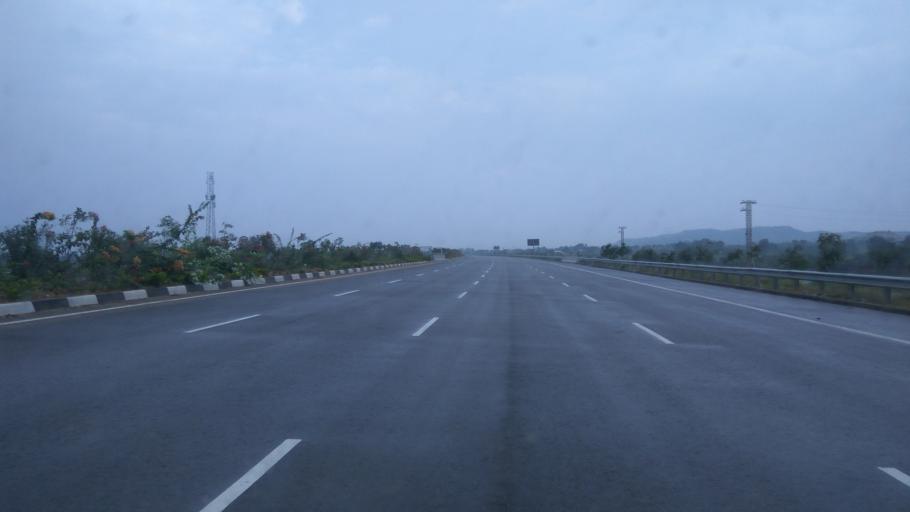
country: IN
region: Telangana
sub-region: Rangareddi
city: Ghatkesar
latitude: 17.4667
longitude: 78.6707
